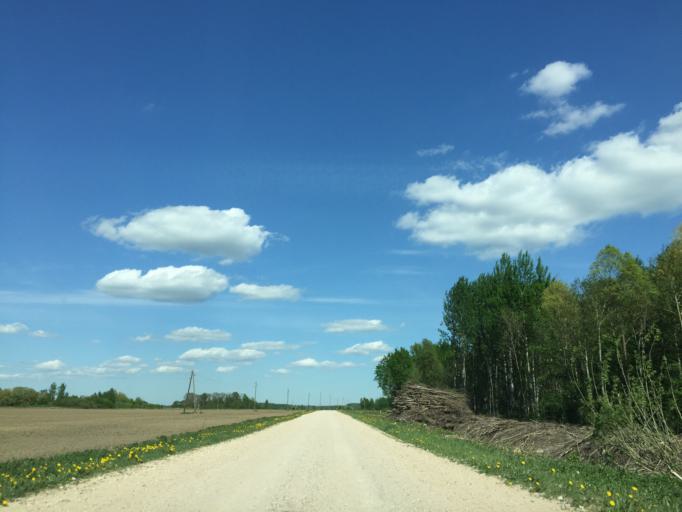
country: LV
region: Rundales
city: Pilsrundale
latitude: 56.3558
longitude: 24.0046
